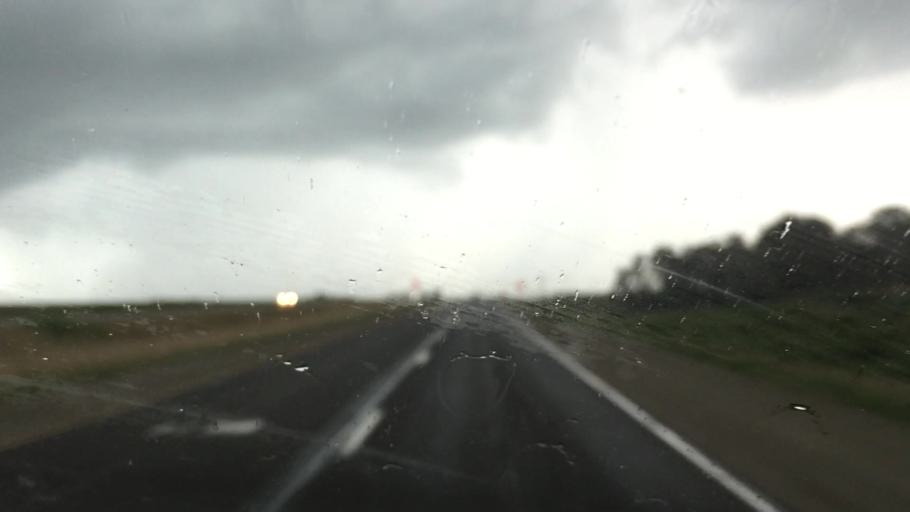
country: US
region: Iowa
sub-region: Henry County
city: Mount Pleasant
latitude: 40.8752
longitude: -91.5649
